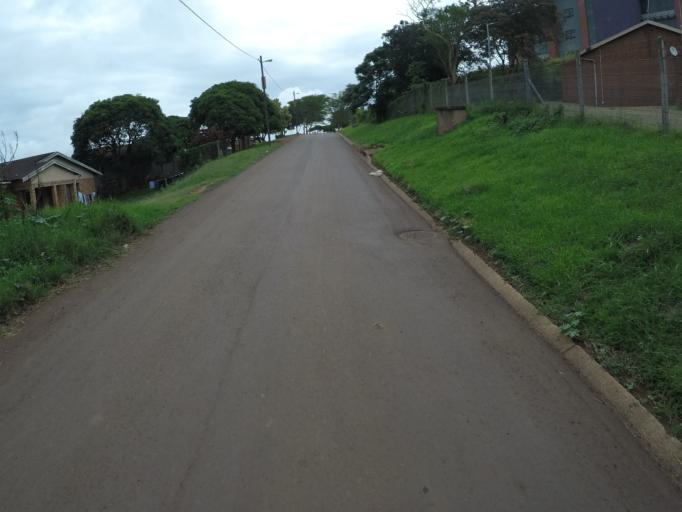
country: ZA
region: KwaZulu-Natal
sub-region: uThungulu District Municipality
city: Empangeni
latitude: -28.7800
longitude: 31.8669
